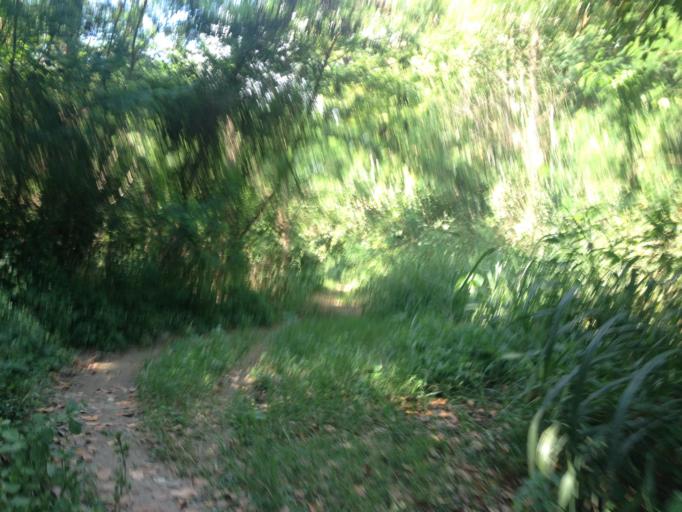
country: TH
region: Chiang Mai
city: Hang Dong
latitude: 18.7287
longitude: 98.9042
